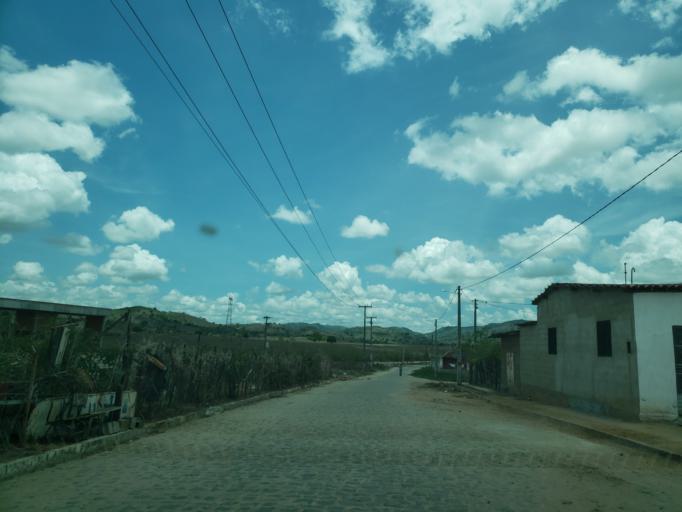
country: BR
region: Alagoas
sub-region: Uniao Dos Palmares
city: Uniao dos Palmares
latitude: -9.1497
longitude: -36.0121
